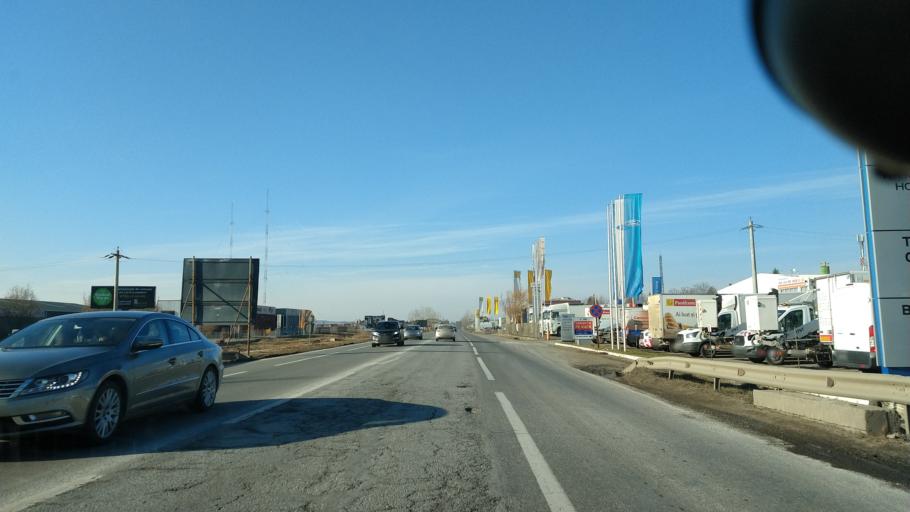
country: RO
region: Iasi
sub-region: Comuna Valea Lupului
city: Valea Lupului
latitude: 47.1820
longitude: 27.4679
